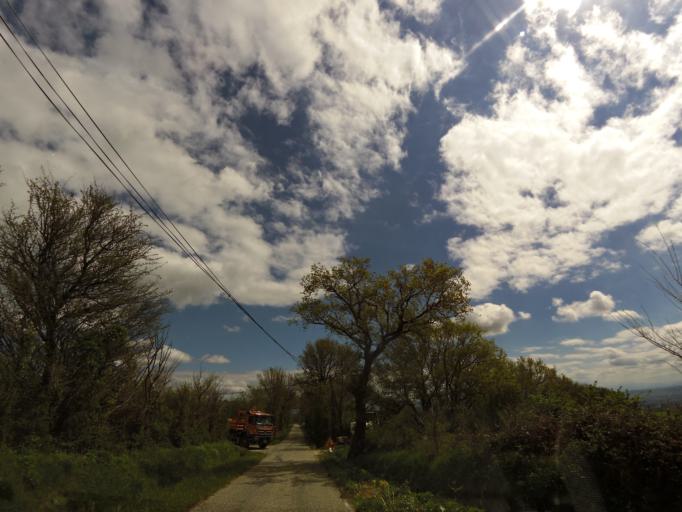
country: FR
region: Midi-Pyrenees
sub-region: Departement du Tarn
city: Soreze
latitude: 43.3727
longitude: 2.0644
